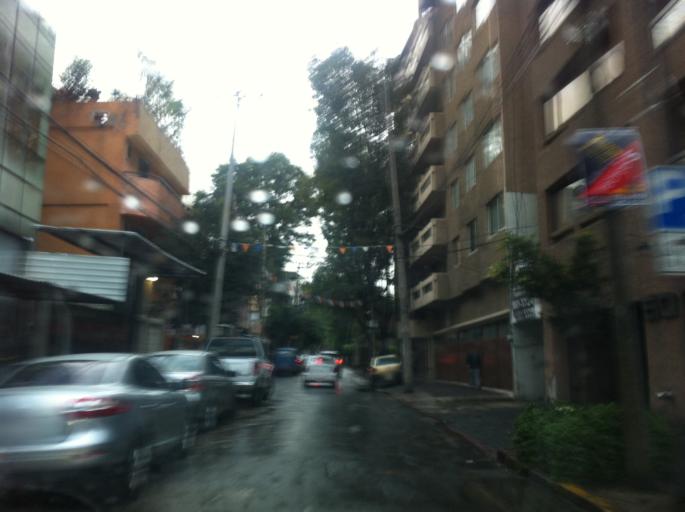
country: MX
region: Mexico City
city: Colonia del Valle
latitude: 19.3703
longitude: -99.1805
